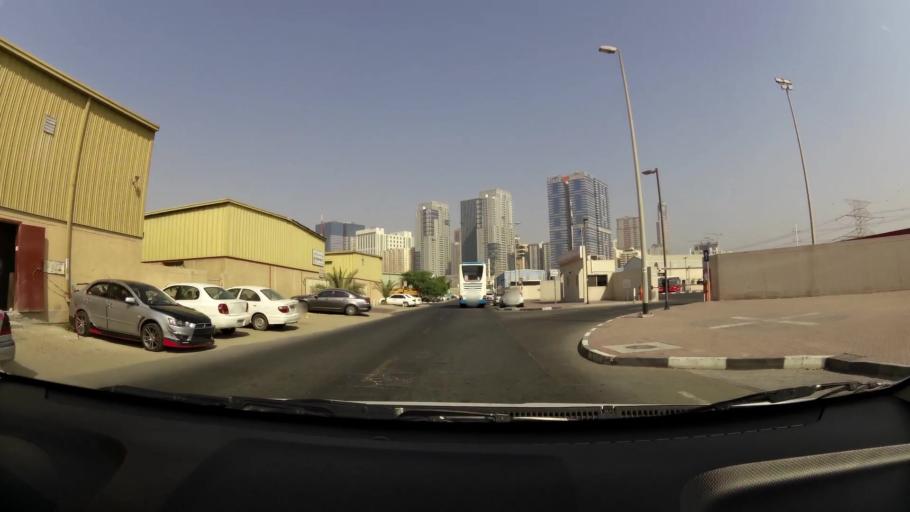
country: AE
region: Ash Shariqah
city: Sharjah
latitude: 25.2988
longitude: 55.3892
